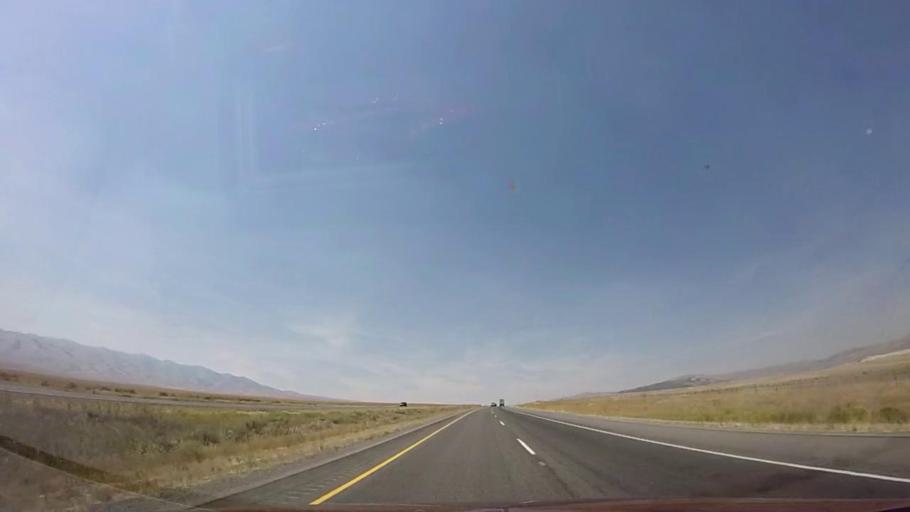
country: US
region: Idaho
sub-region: Power County
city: American Falls
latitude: 42.1273
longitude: -112.9659
